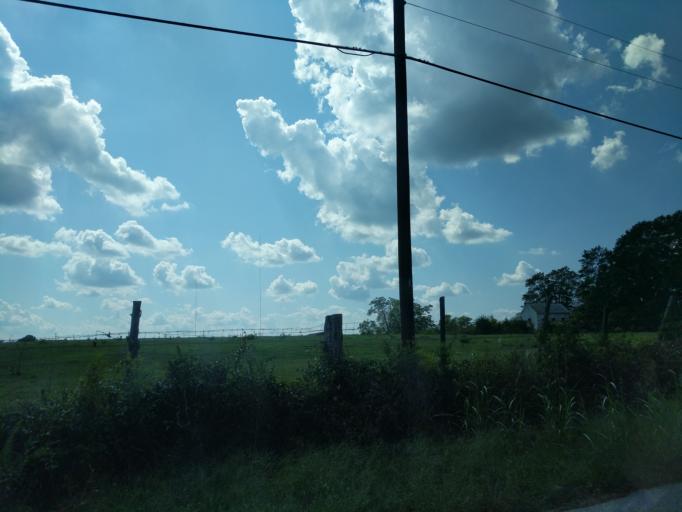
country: US
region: South Carolina
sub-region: Laurens County
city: Laurens
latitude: 34.5800
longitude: -82.0984
